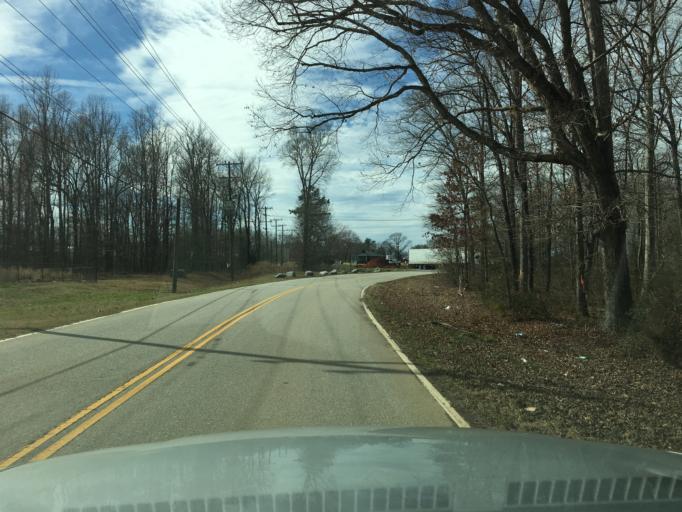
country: US
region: South Carolina
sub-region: Spartanburg County
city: Duncan
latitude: 34.9036
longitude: -82.1643
